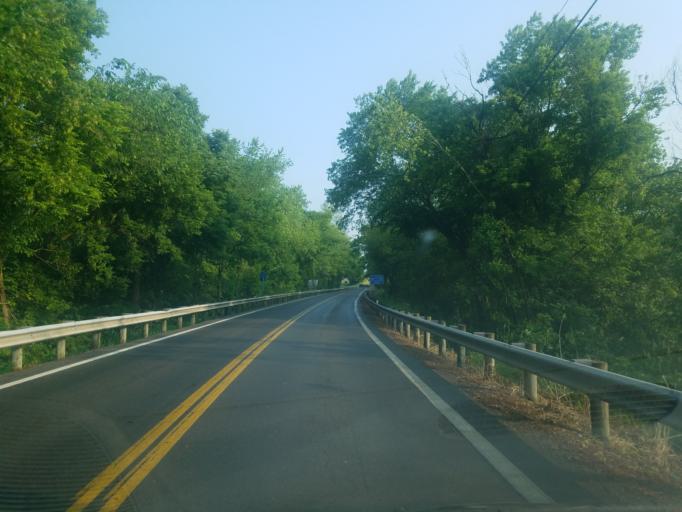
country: US
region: Ohio
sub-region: Tuscarawas County
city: Dover
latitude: 40.5801
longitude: -81.3934
